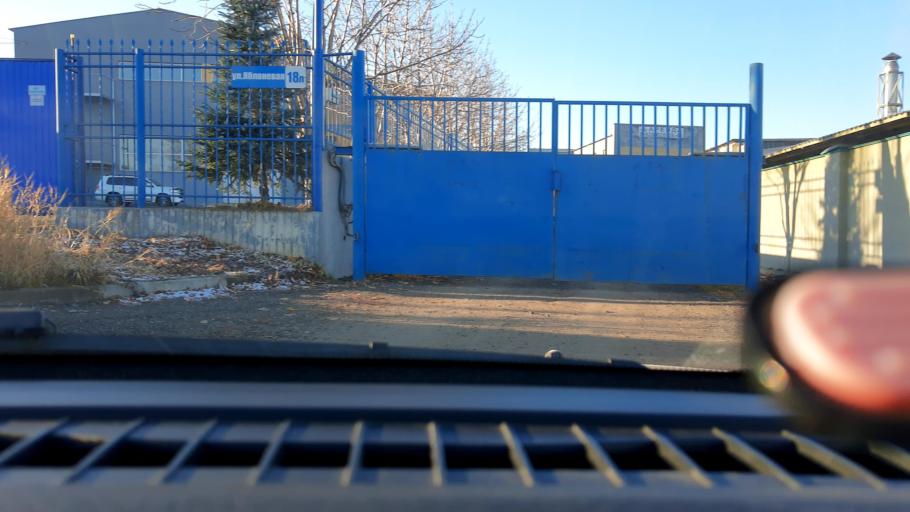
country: RU
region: Nizjnij Novgorod
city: Bor
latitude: 56.3101
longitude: 44.0572
